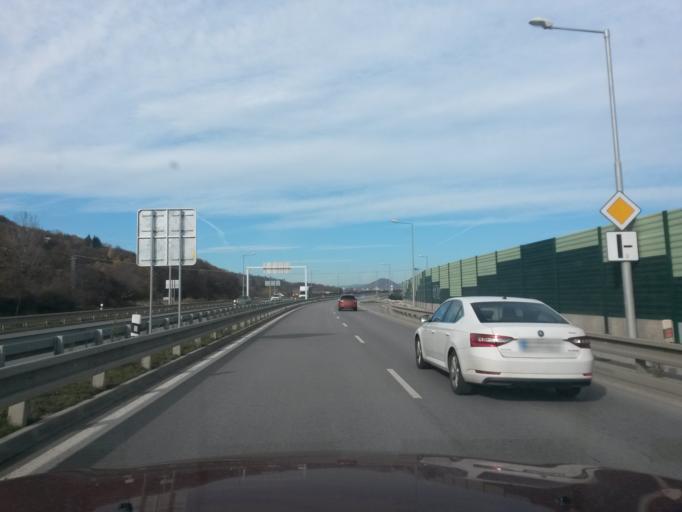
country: SK
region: Presovsky
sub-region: Okres Presov
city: Presov
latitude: 48.9769
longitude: 21.2421
